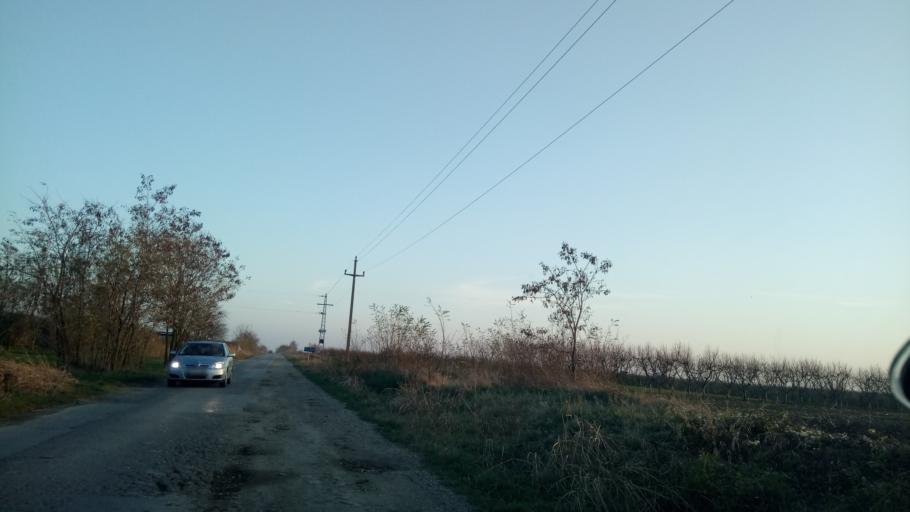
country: RS
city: Novi Slankamen
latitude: 45.1228
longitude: 20.2643
